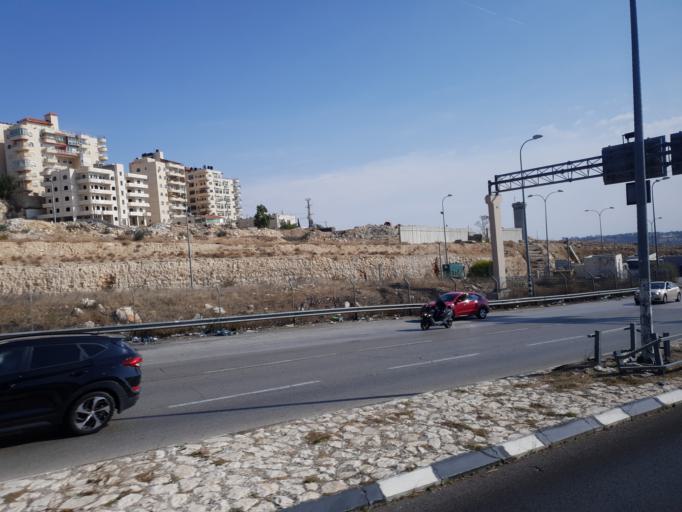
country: PS
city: Az Za`ayyim
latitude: 31.7837
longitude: 35.2624
